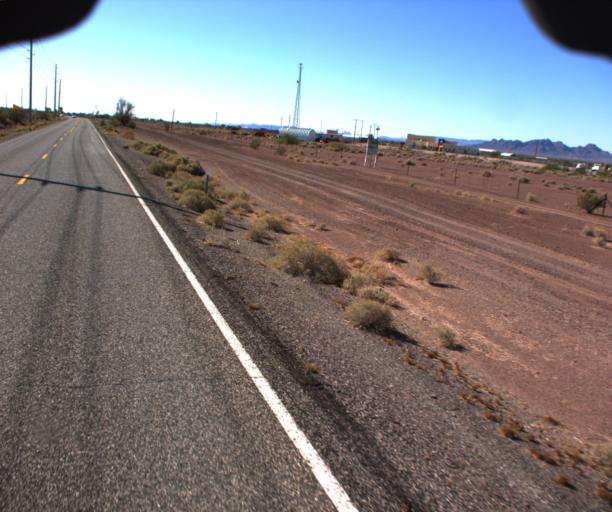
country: US
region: Arizona
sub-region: La Paz County
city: Quartzsite
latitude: 33.9164
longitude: -113.9934
